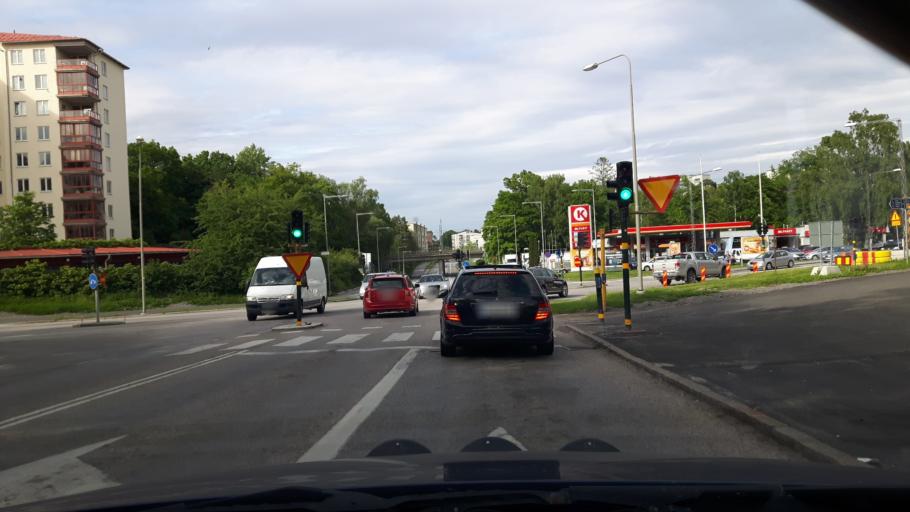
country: SE
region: Stockholm
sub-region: Stockholms Kommun
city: Arsta
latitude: 59.2353
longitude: 18.0957
